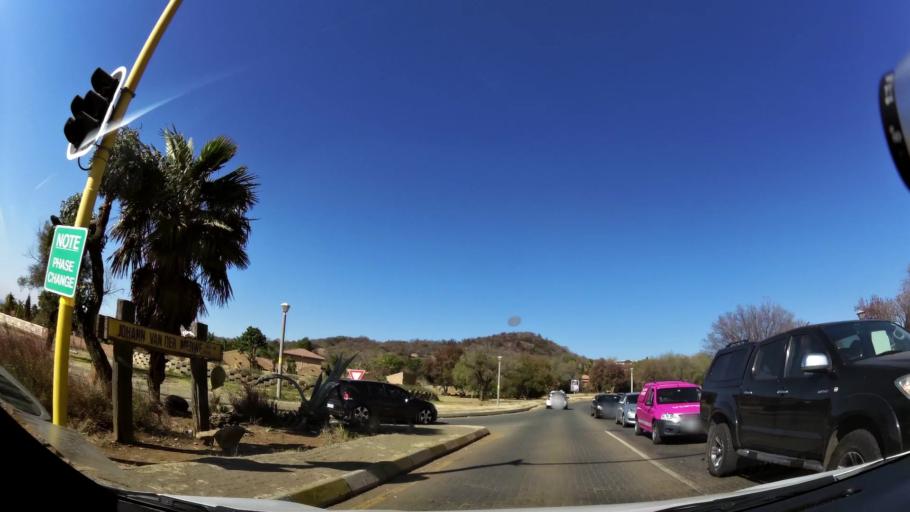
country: ZA
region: Gauteng
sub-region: Ekurhuleni Metropolitan Municipality
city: Germiston
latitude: -26.2876
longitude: 28.0951
